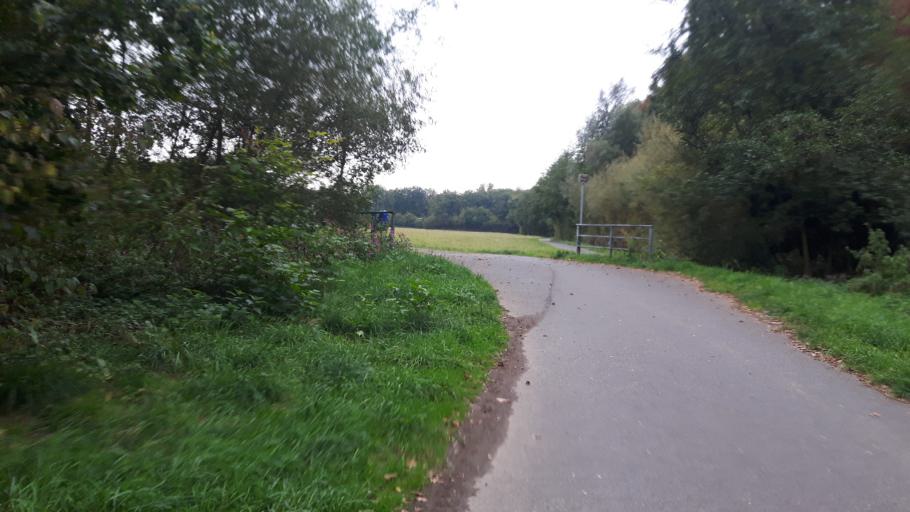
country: DE
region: North Rhine-Westphalia
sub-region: Regierungsbezirk Koln
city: Hennef
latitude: 50.7767
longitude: 7.3176
